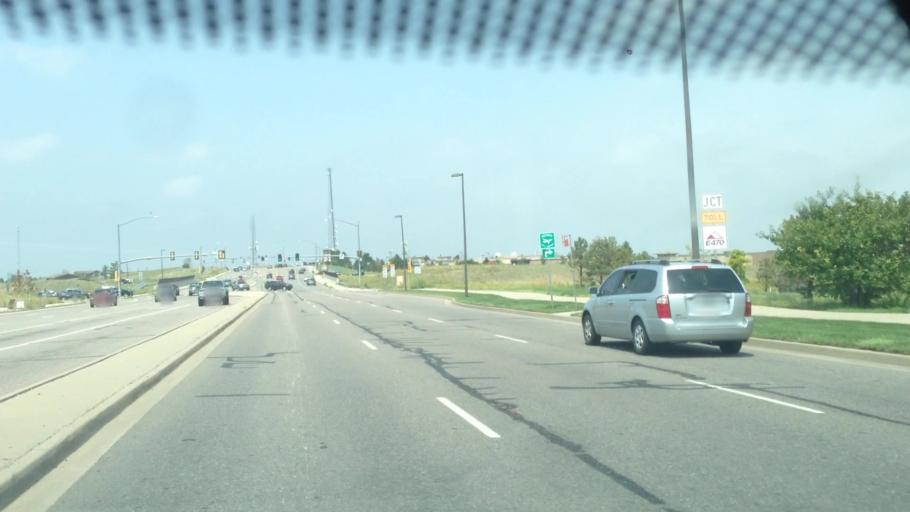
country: US
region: Colorado
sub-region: Douglas County
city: Parker
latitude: 39.6001
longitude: -104.7115
